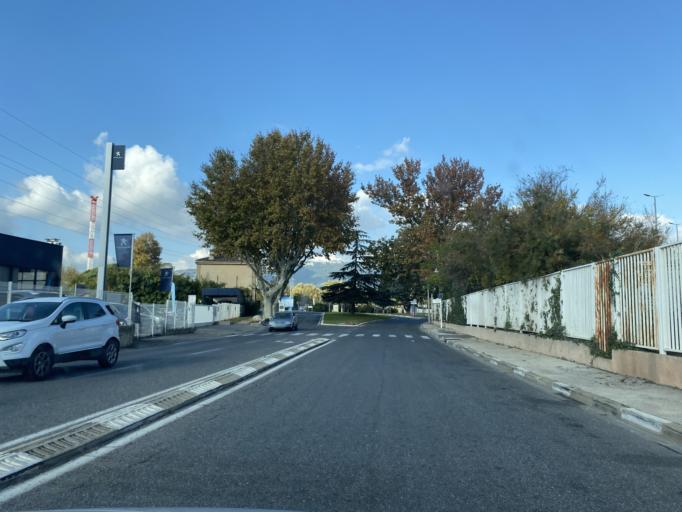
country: FR
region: Provence-Alpes-Cote d'Azur
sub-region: Departement du Var
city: La Seyne-sur-Mer
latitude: 43.1159
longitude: 5.8785
